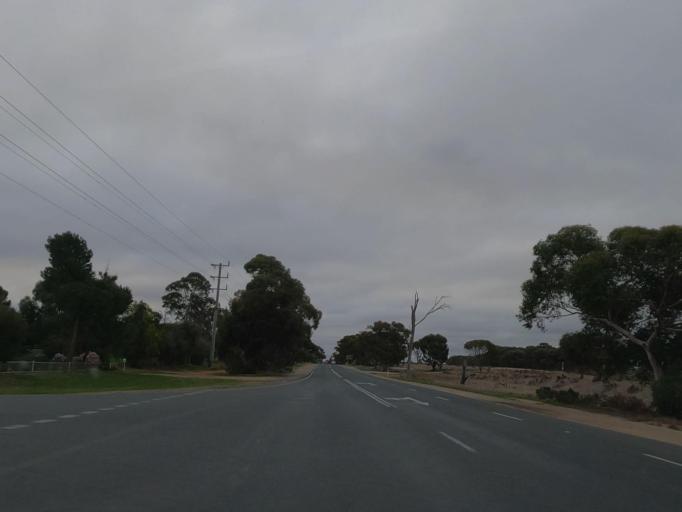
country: AU
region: Victoria
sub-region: Swan Hill
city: Swan Hill
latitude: -35.3854
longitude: 143.5670
